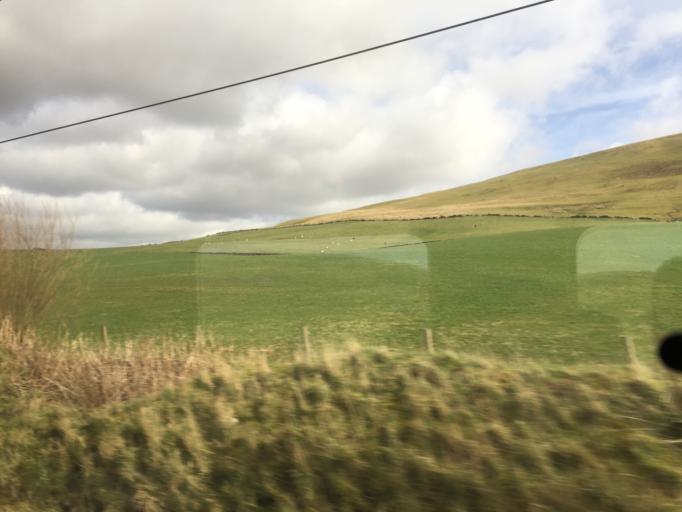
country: GB
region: Scotland
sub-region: South Lanarkshire
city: Douglas
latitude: 55.5102
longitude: -3.6855
